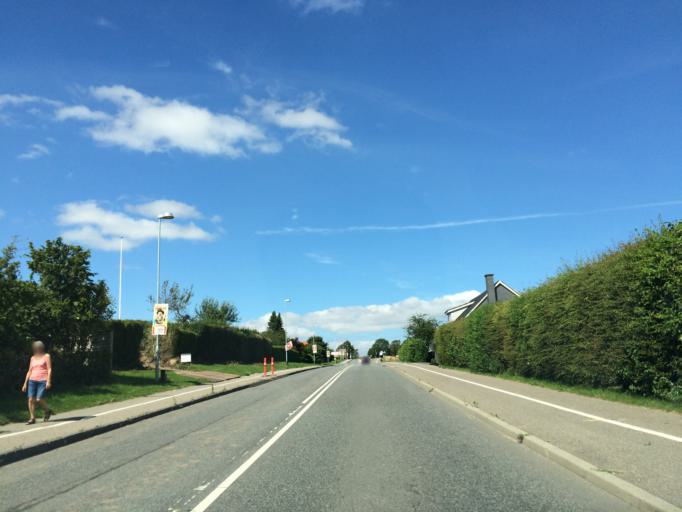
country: DK
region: Central Jutland
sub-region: Arhus Kommune
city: Logten
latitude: 56.2676
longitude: 10.3097
